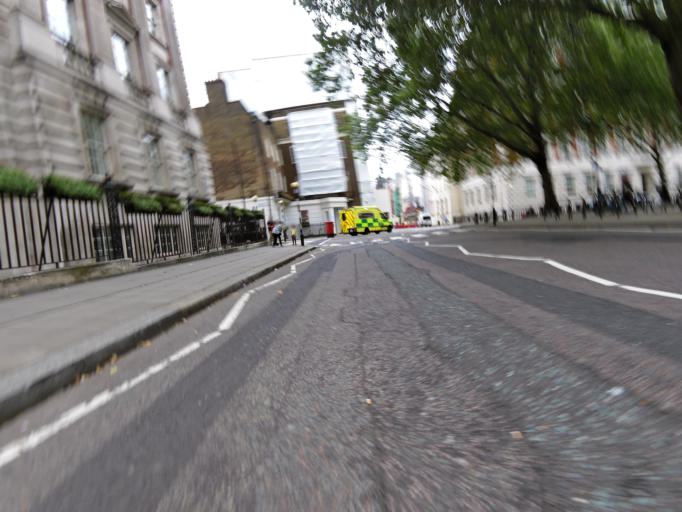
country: GB
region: England
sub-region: Greater London
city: London
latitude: 51.5123
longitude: -0.1509
